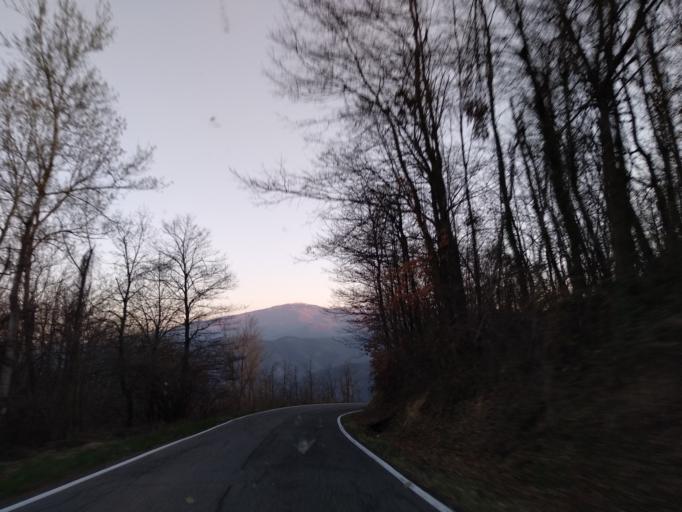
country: IT
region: Emilia-Romagna
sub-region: Provincia di Reggio Emilia
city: Castelnovo ne'Monti
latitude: 44.4103
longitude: 10.3987
